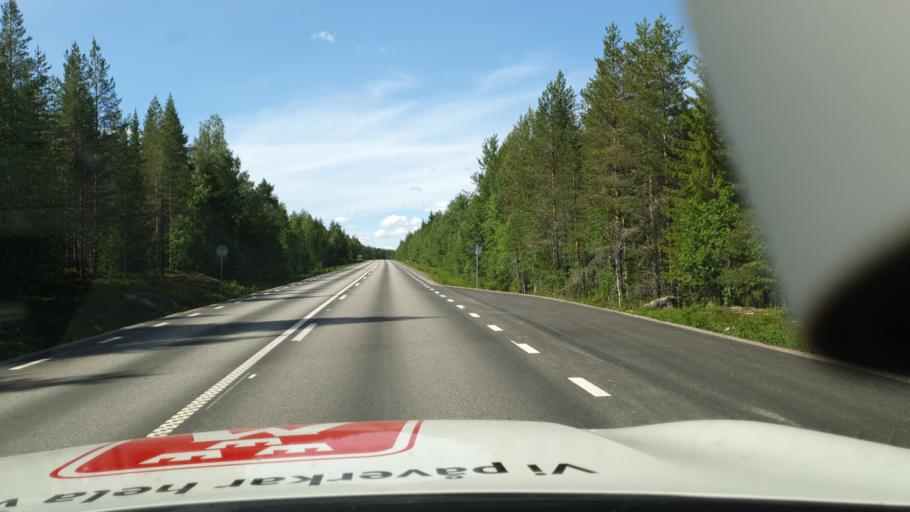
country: SE
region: Vaesterbotten
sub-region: Skelleftea Kommun
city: Boliden
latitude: 64.8817
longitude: 20.3915
